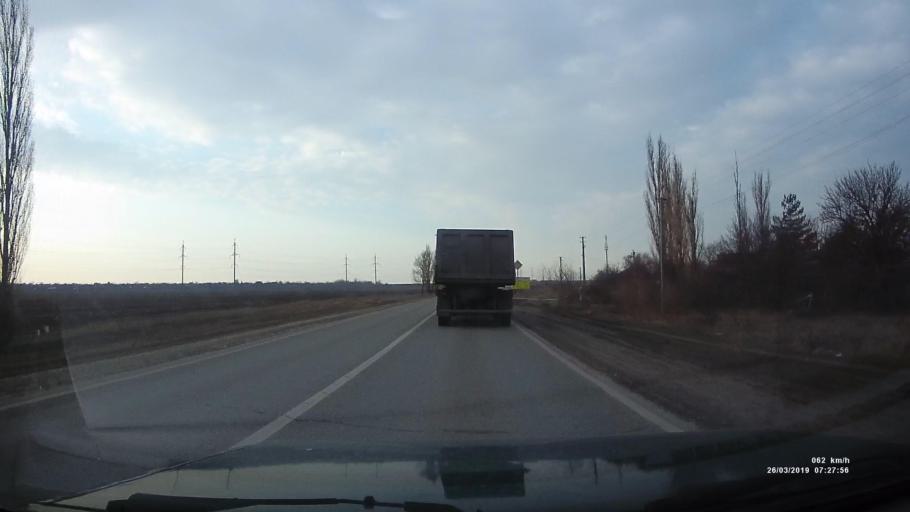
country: RU
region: Rostov
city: Taganrog
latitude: 47.2582
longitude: 38.8259
